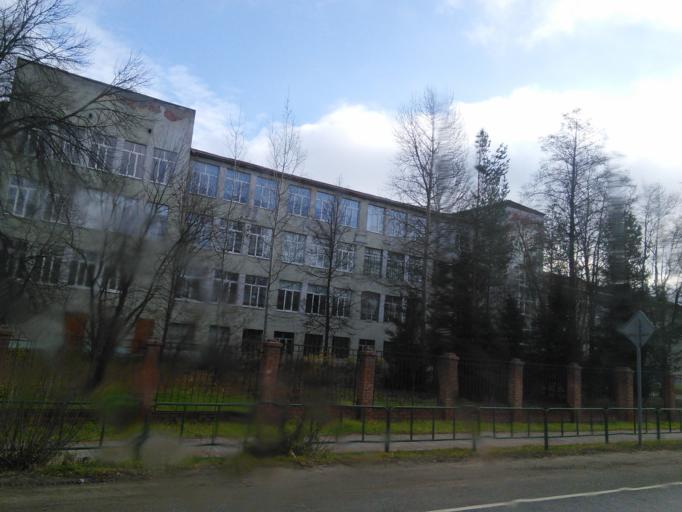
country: RU
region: Moskovskaya
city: Likino-Dulevo
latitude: 55.7116
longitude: 38.9578
